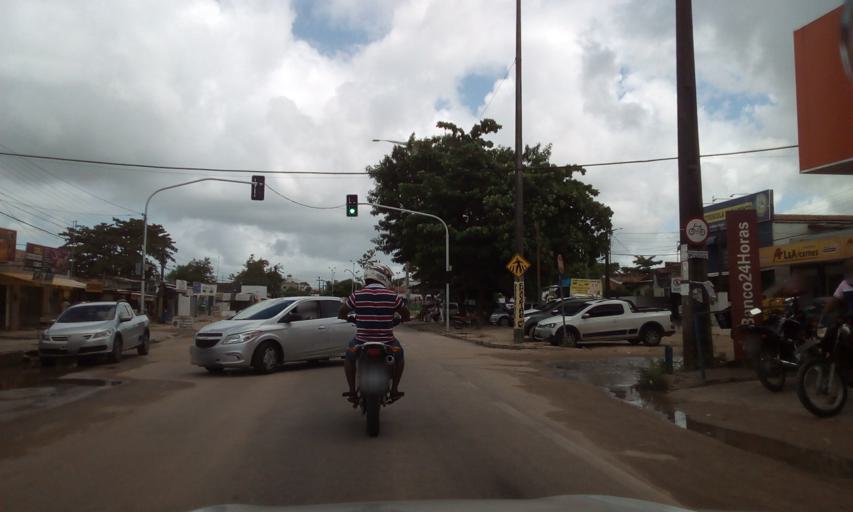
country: BR
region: Paraiba
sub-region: Conde
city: Conde
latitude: -7.2048
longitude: -34.8502
